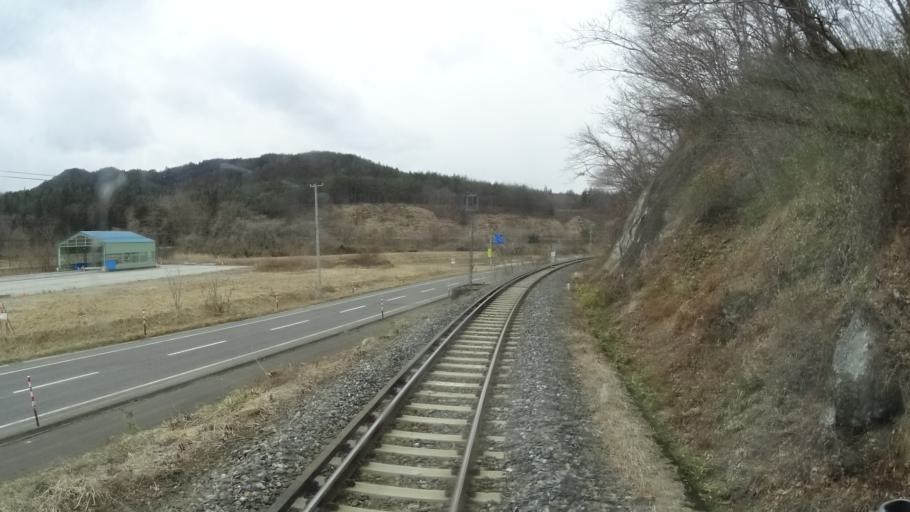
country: JP
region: Iwate
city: Tono
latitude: 39.3000
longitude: 141.3973
